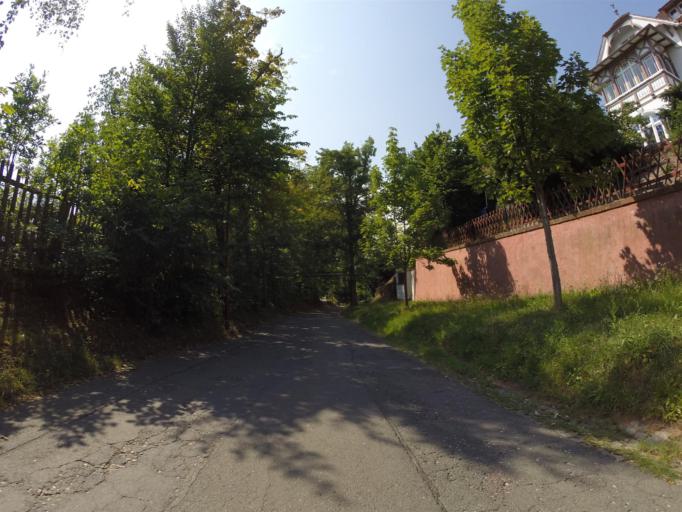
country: DE
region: Thuringia
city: Stadtroda
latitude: 50.8588
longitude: 11.7330
